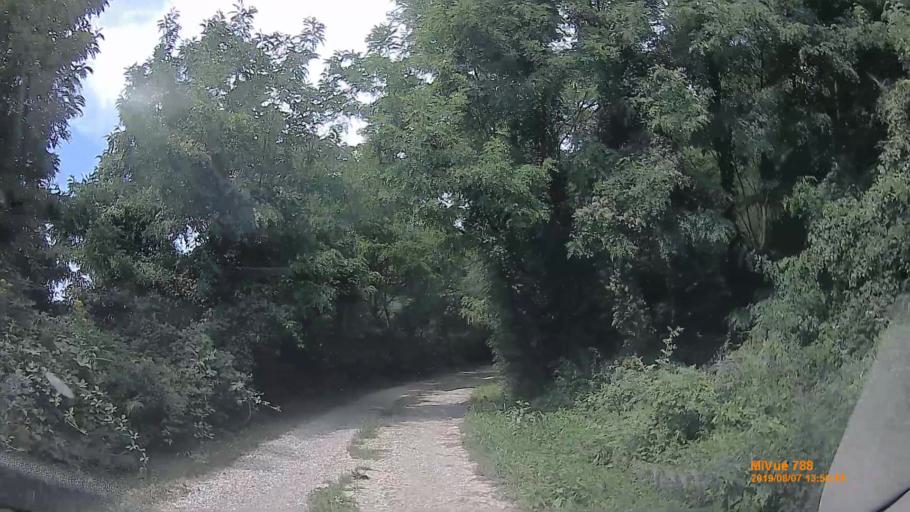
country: HU
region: Zala
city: Cserszegtomaj
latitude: 46.8942
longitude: 17.1762
